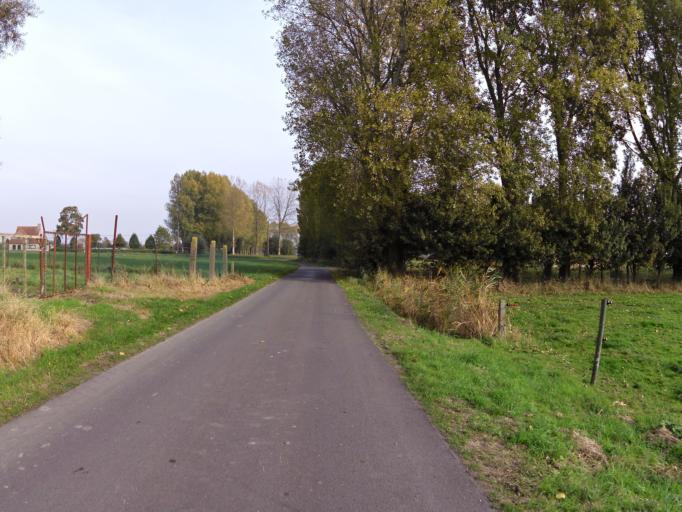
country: BE
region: Flanders
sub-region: Provincie West-Vlaanderen
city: Oudenburg
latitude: 51.1540
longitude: 2.9982
